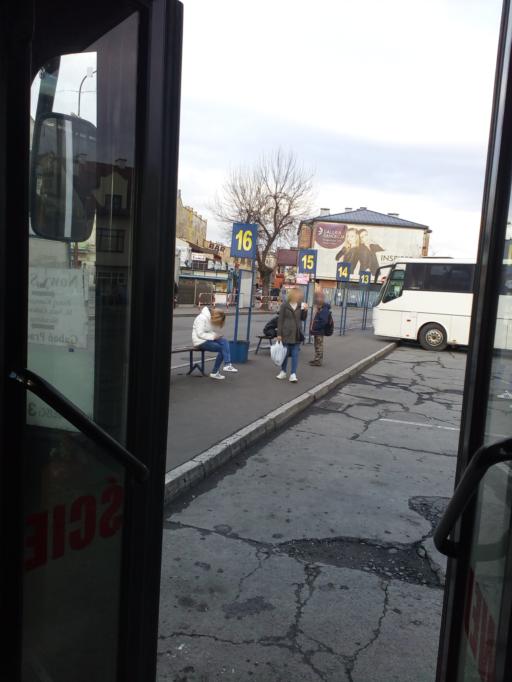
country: PL
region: Lesser Poland Voivodeship
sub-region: Powiat nowosadecki
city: Nowy Sacz
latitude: 49.6174
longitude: 20.6982
